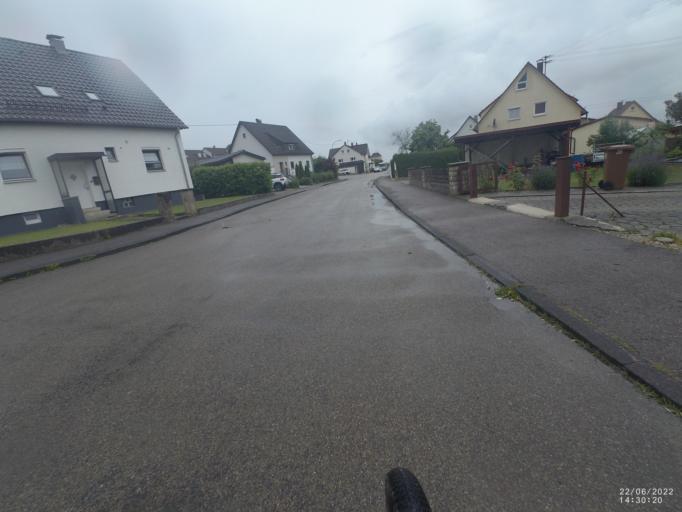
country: DE
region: Baden-Wuerttemberg
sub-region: Regierungsbezirk Stuttgart
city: Gerstetten
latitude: 48.6238
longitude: 10.0320
